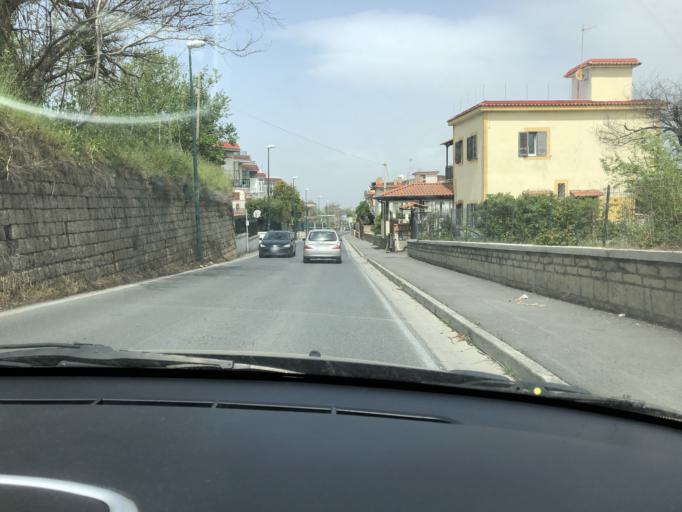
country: IT
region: Campania
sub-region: Provincia di Napoli
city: Torre Caracciolo
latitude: 40.8732
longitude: 14.1871
